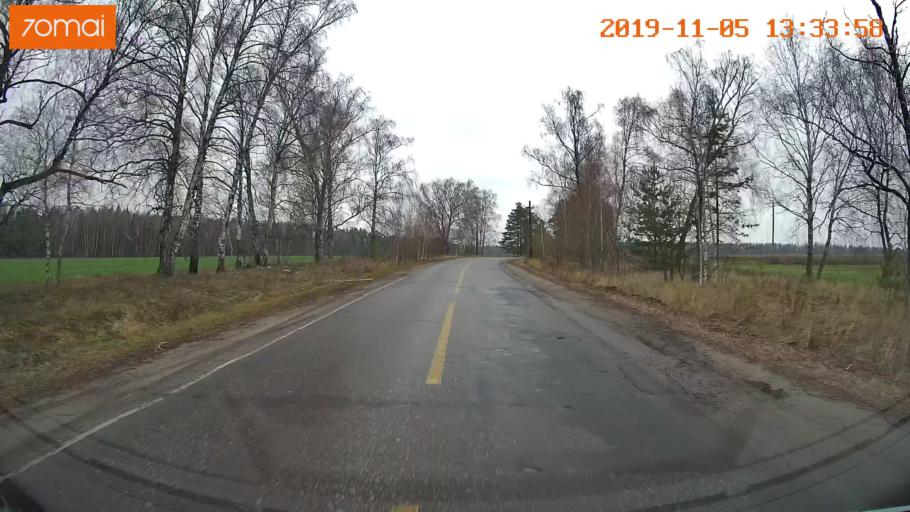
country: RU
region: Ivanovo
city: Shuya
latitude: 56.8967
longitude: 41.3905
